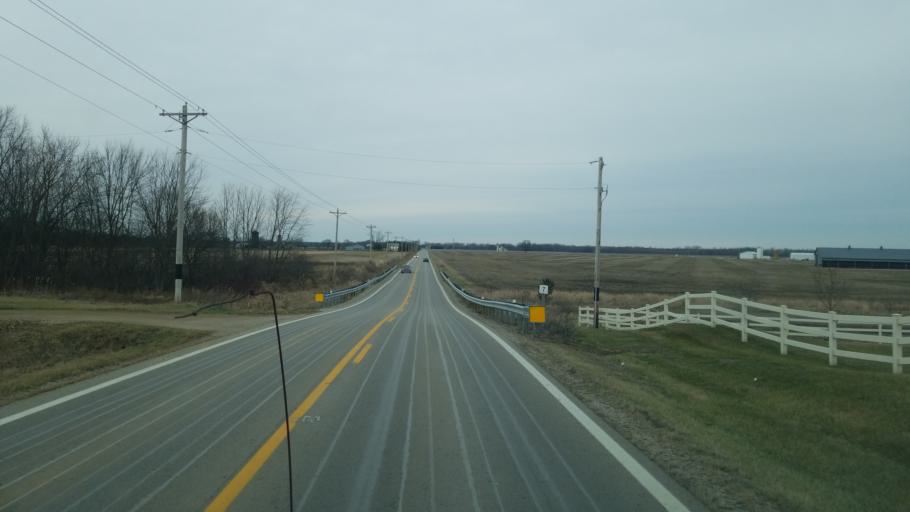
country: US
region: Ohio
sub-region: Pickaway County
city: Circleville
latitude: 39.6014
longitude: -83.0040
